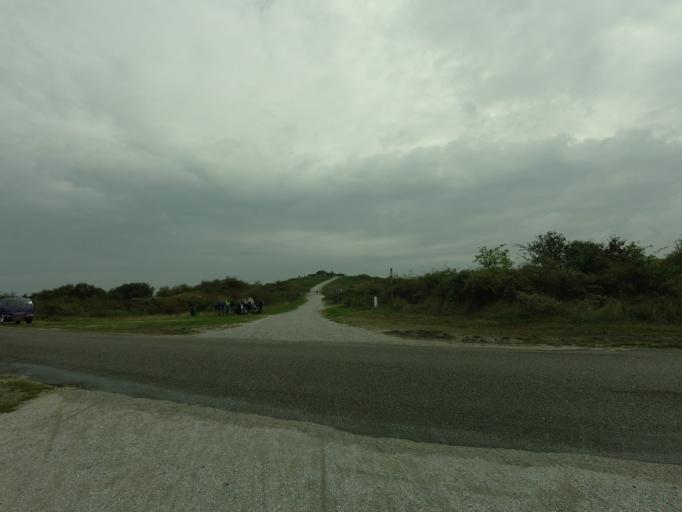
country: NL
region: Friesland
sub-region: Gemeente Schiermonnikoog
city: Schiermonnikoog
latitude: 53.4869
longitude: 6.1795
